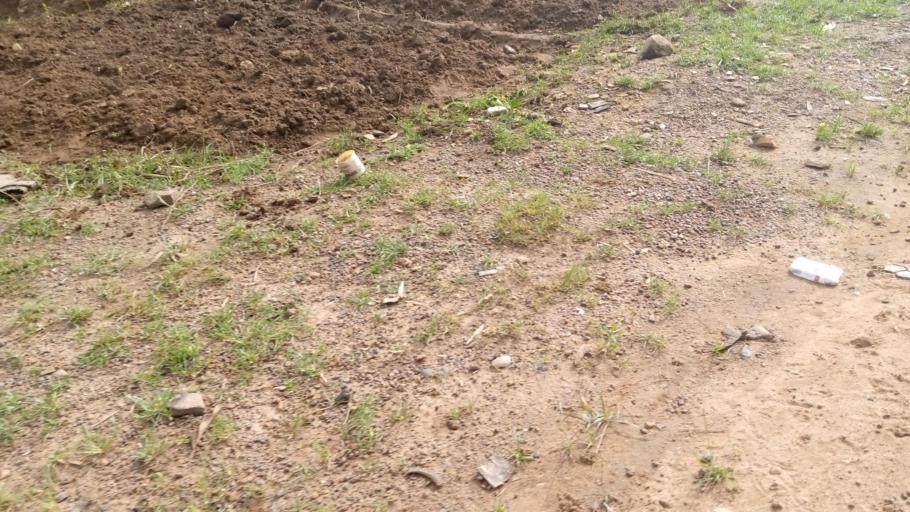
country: SL
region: Southern Province
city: Pujehun
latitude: 7.3487
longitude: -11.7191
